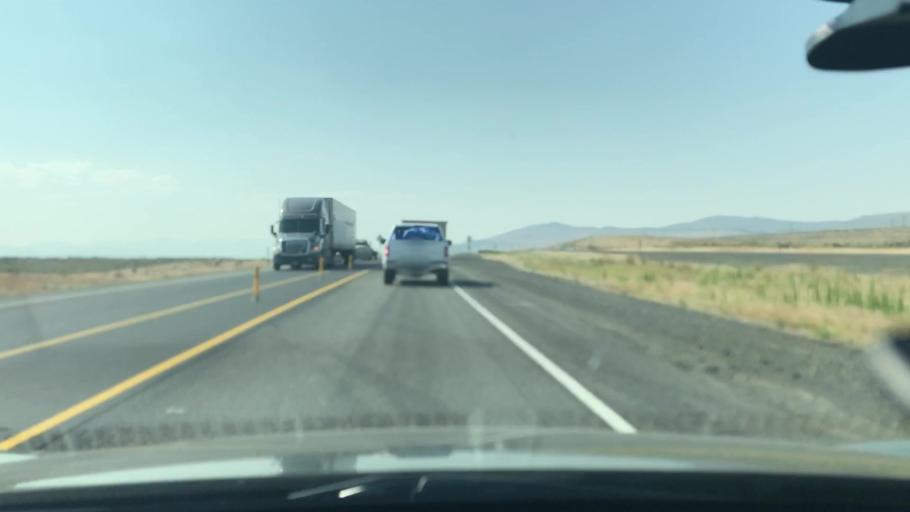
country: US
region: Oregon
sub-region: Baker County
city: Baker City
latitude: 44.6904
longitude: -117.6846
